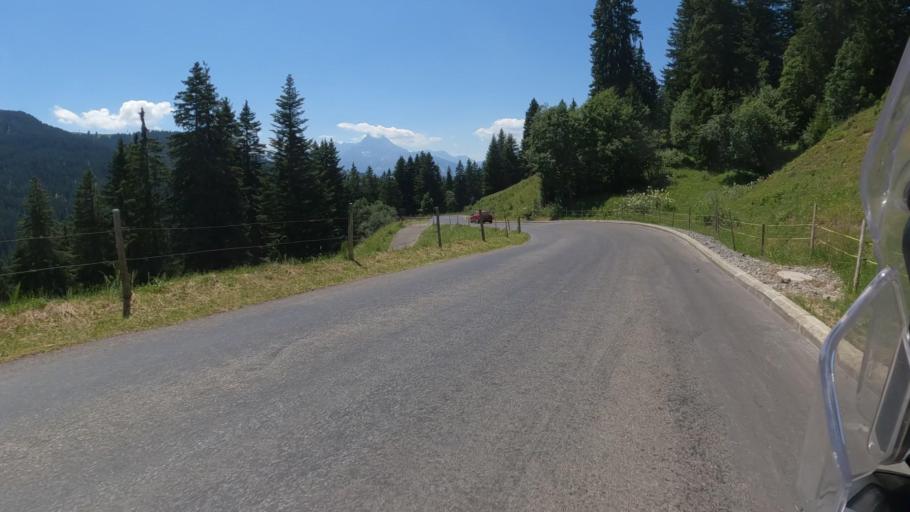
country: CH
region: Vaud
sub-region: Aigle District
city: Villars-sur-Ollon
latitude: 46.3144
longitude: 7.1095
